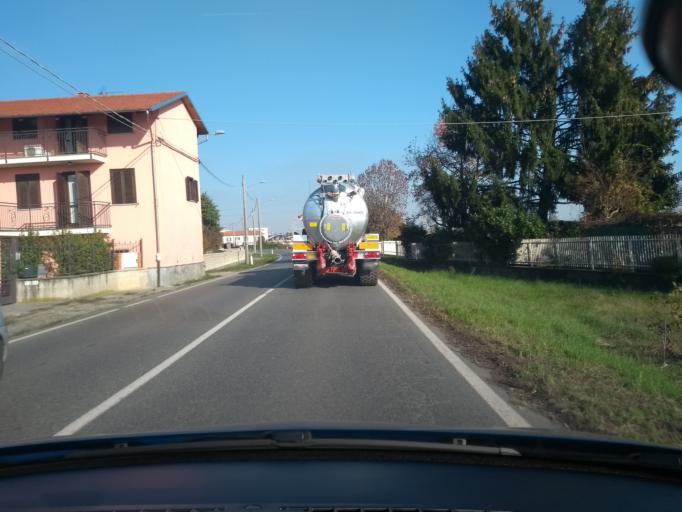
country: IT
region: Piedmont
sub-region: Provincia di Torino
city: Cirie
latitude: 45.2181
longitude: 7.5958
